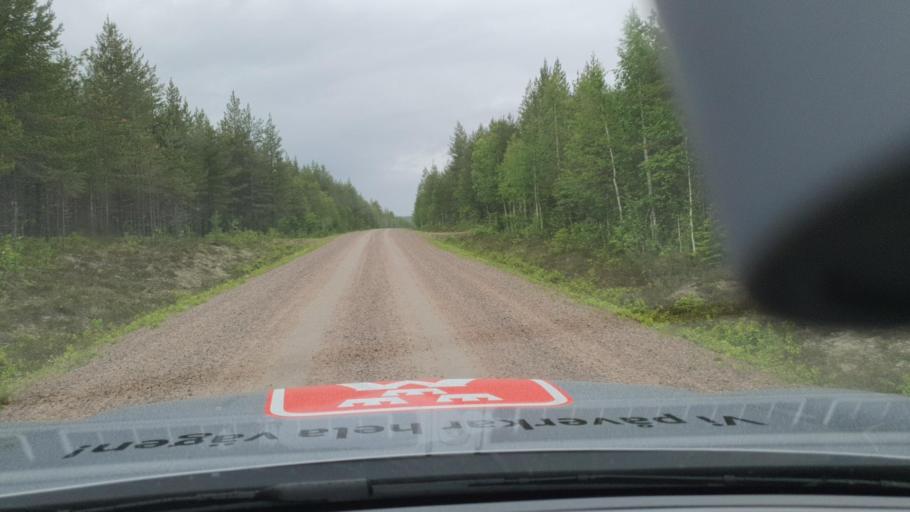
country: SE
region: Norrbotten
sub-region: Overkalix Kommun
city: OEverkalix
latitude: 66.5734
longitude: 22.7464
